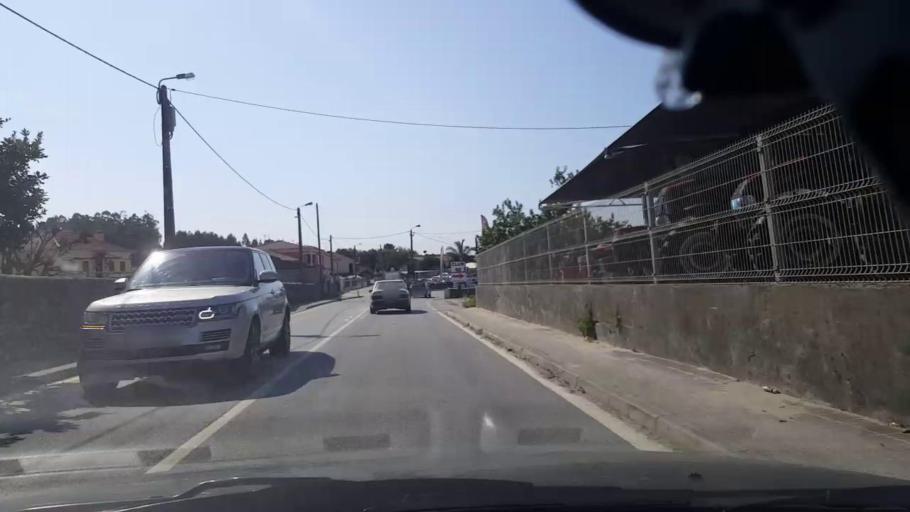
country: PT
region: Porto
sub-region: Povoa de Varzim
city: Pedroso
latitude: 41.3992
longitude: -8.6835
